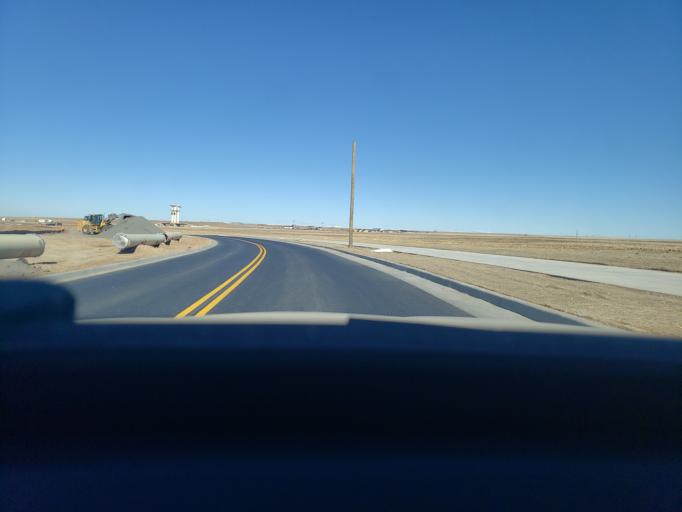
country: US
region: Colorado
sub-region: Adams County
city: Aurora
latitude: 39.7626
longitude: -104.7116
